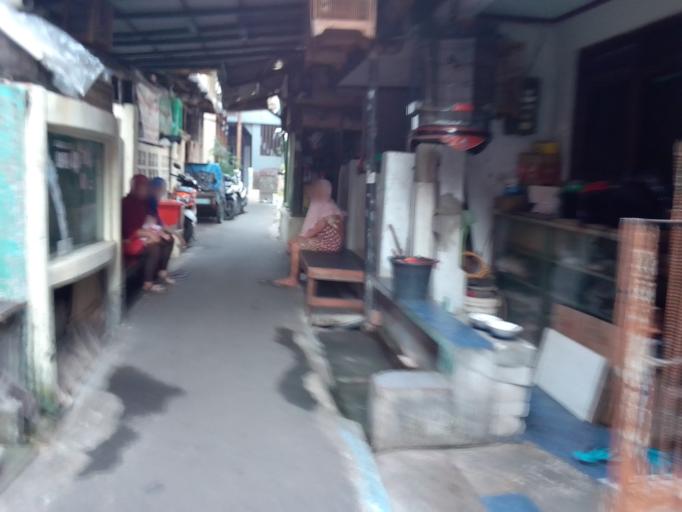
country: ID
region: Jakarta Raya
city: Jakarta
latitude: -6.1803
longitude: 106.8141
